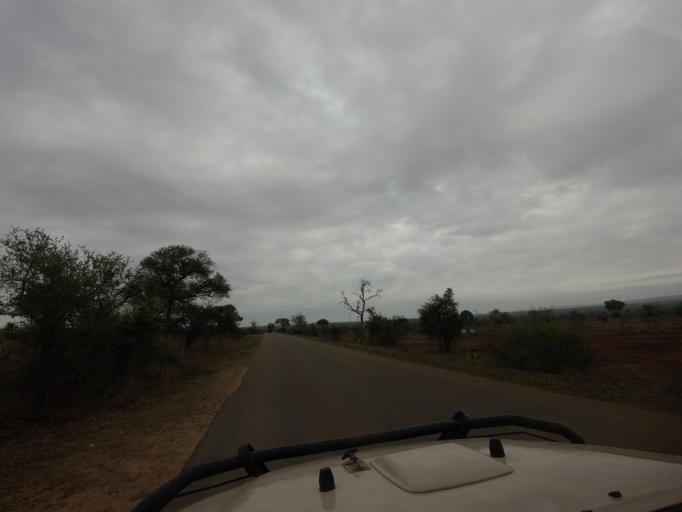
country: ZA
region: Mpumalanga
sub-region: Ehlanzeni District
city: Komatipoort
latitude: -25.3483
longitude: 31.8840
